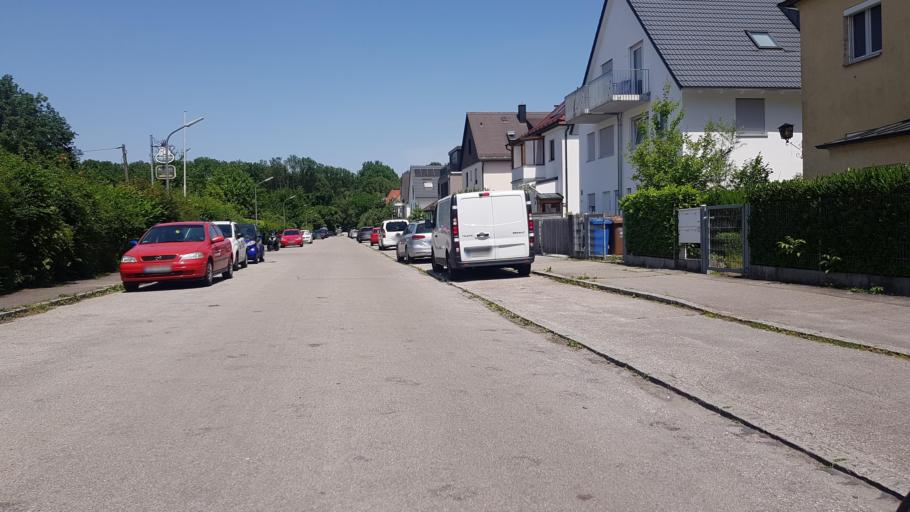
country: DE
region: Bavaria
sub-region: Upper Bavaria
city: Unterfoehring
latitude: 48.1956
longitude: 11.6285
